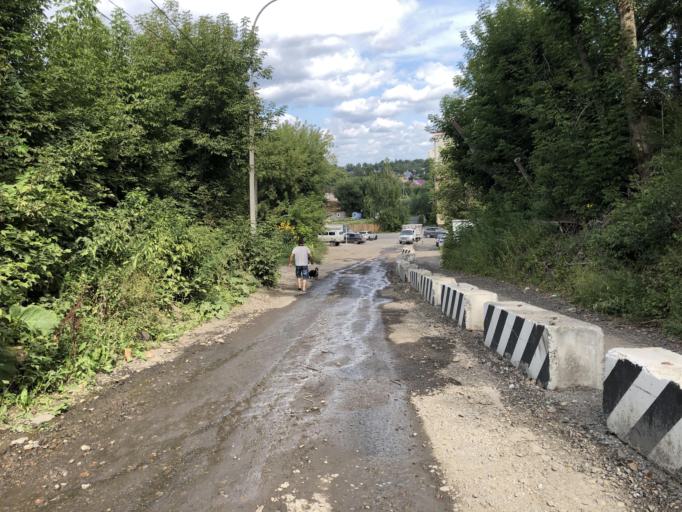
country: RU
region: Tomsk
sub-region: Tomskiy Rayon
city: Tomsk
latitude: 56.4807
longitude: 84.9621
